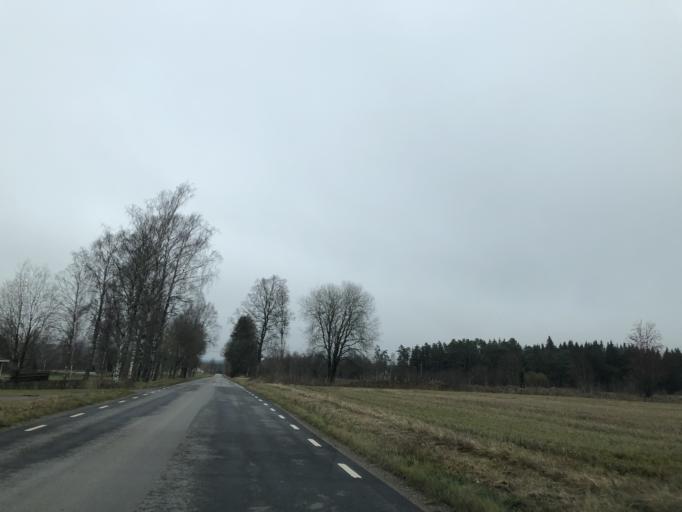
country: SE
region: Vaestra Goetaland
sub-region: Ulricehamns Kommun
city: Ulricehamn
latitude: 57.6832
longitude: 13.4734
